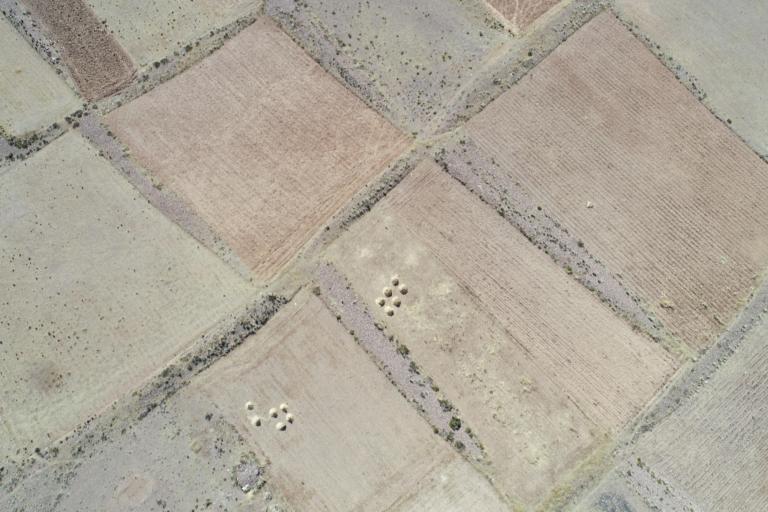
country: BO
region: La Paz
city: Achacachi
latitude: -15.8983
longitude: -68.9005
